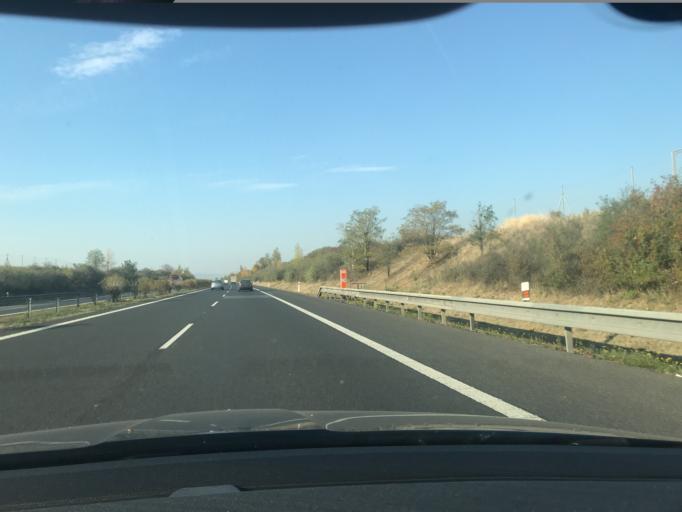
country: CZ
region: Ustecky
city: Roudnice nad Labem
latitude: 50.4085
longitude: 14.2184
